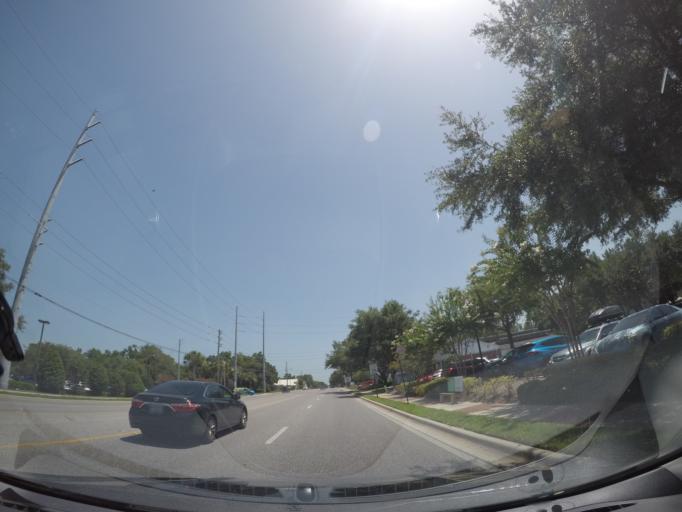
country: US
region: Florida
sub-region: Orange County
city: Apopka
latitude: 28.6811
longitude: -81.5095
